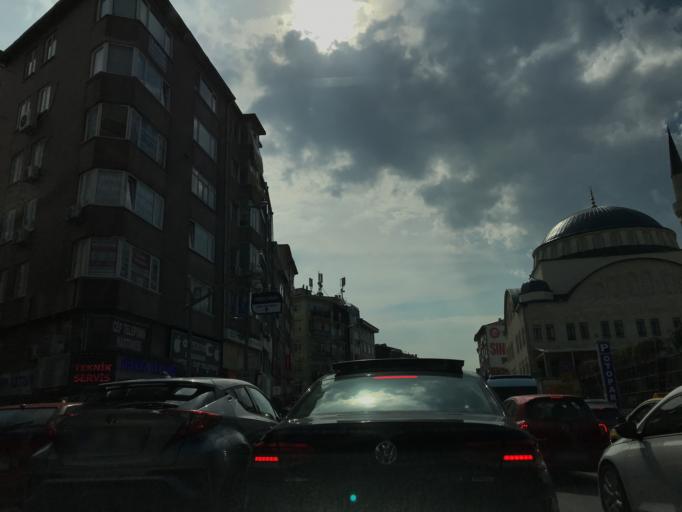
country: TR
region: Istanbul
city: UEskuedar
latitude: 40.9924
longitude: 29.0344
